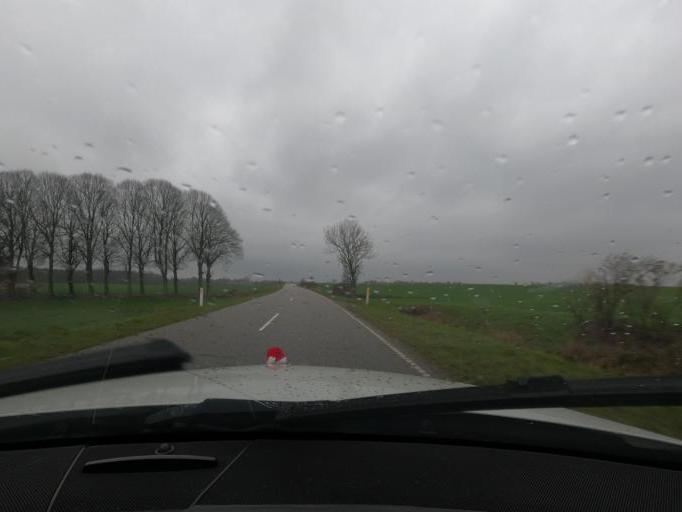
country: DK
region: South Denmark
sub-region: Haderslev Kommune
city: Starup
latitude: 55.2396
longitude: 9.6545
